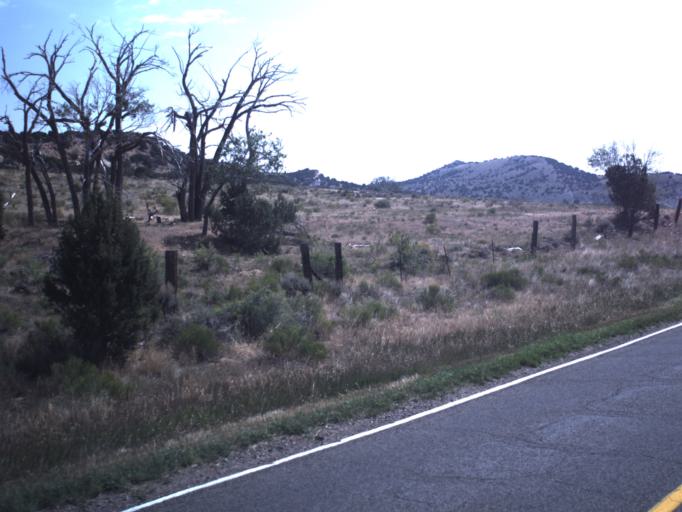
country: US
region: Utah
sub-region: Daggett County
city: Manila
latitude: 40.9769
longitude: -109.7768
